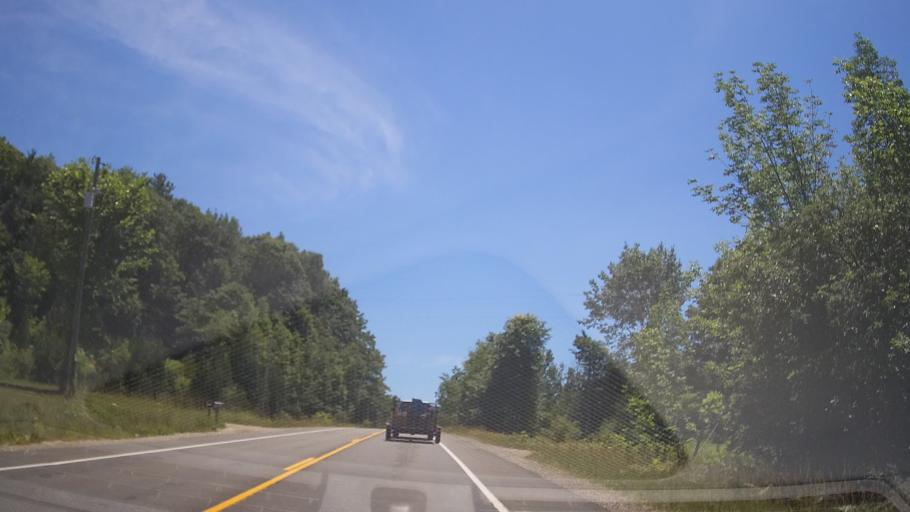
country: US
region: Michigan
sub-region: Grand Traverse County
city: Traverse City
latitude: 44.6254
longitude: -85.6965
